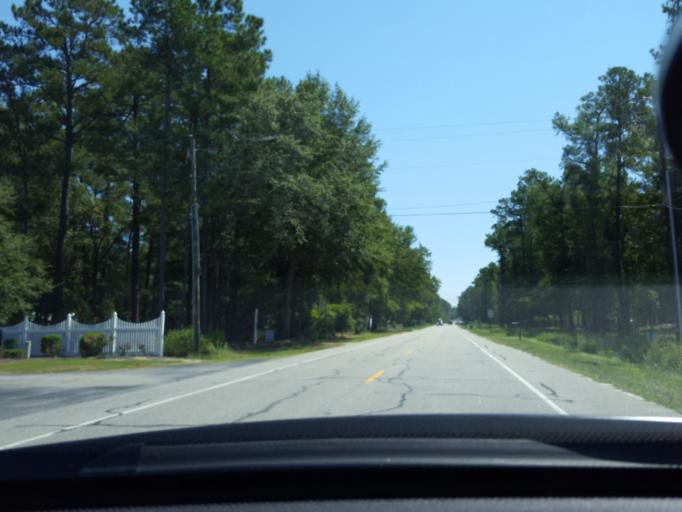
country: US
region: North Carolina
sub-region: Bladen County
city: Elizabethtown
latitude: 34.6313
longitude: -78.5030
